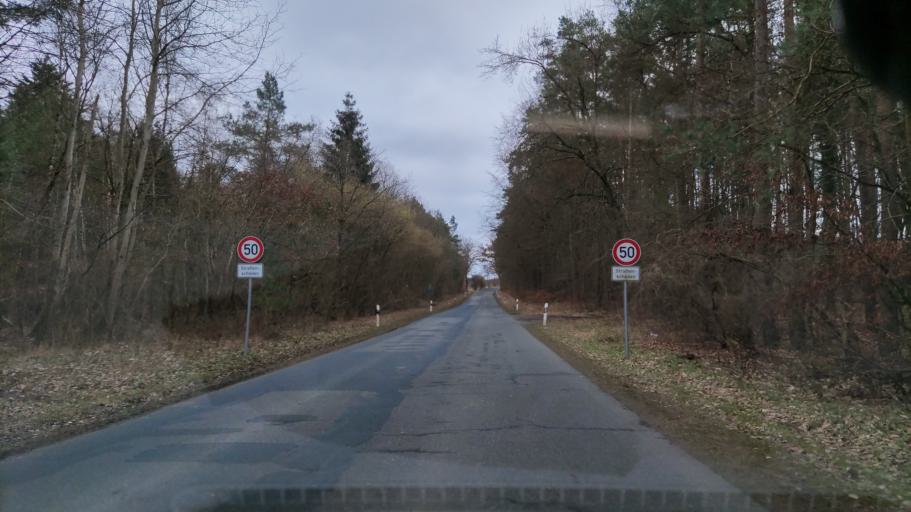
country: DE
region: Lower Saxony
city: Bleckede
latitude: 53.2655
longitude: 10.7263
